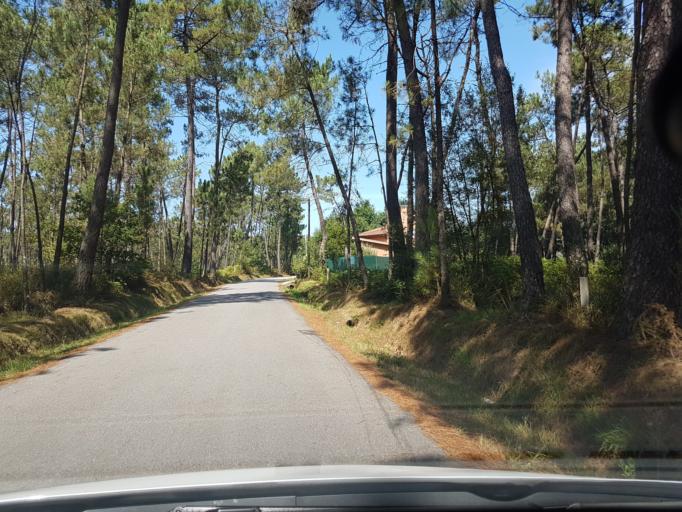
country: ES
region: Galicia
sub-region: Provincia de Pontevedra
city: Porrino
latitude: 42.2073
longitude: -8.6241
